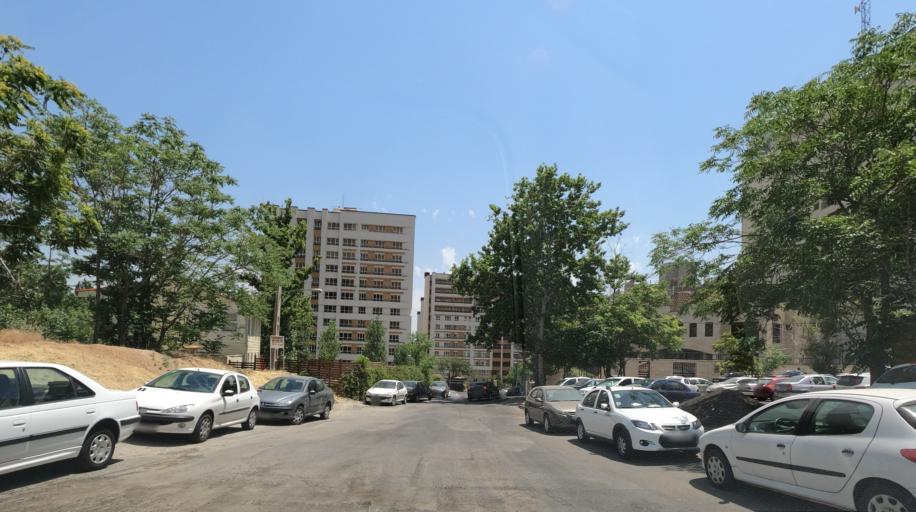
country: IR
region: Tehran
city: Tajrish
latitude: 35.7903
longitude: 51.3852
